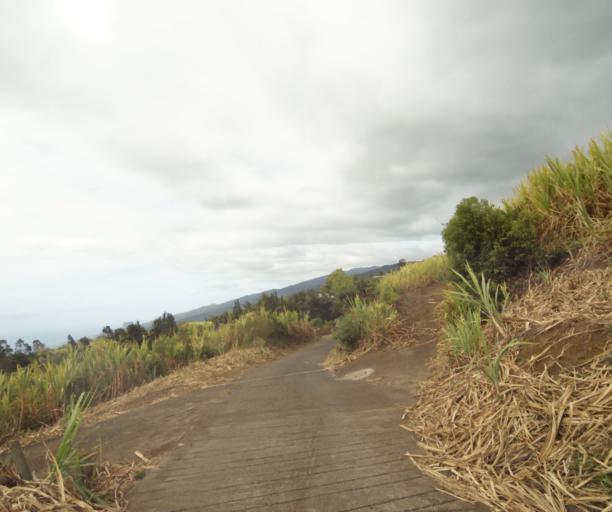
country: RE
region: Reunion
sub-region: Reunion
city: Saint-Paul
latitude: -21.0190
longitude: 55.3259
